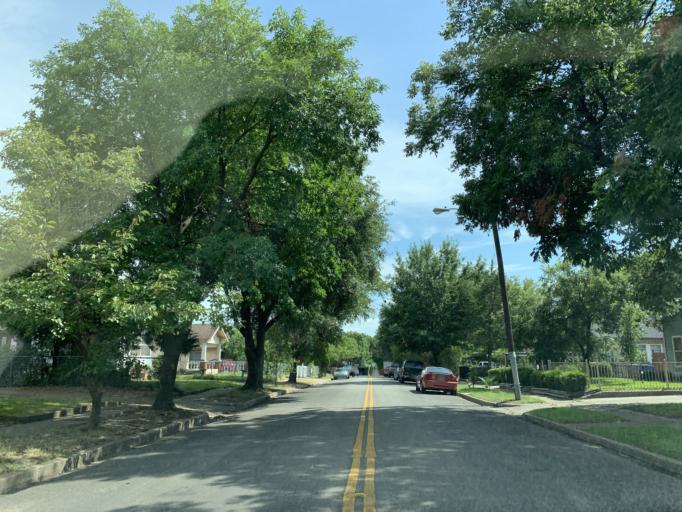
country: US
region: Texas
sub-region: Dallas County
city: Cockrell Hill
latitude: 32.7384
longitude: -96.8405
